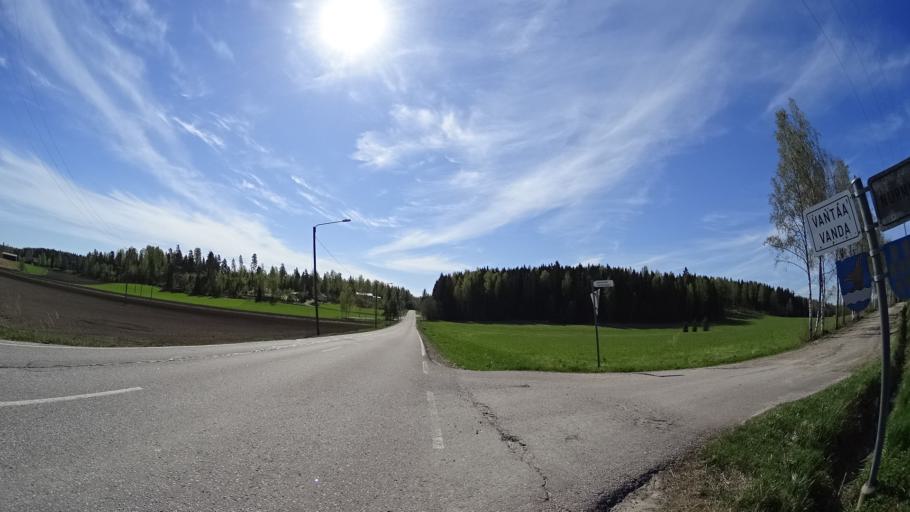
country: FI
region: Uusimaa
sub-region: Helsinki
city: Nurmijaervi
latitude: 60.3945
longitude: 24.8305
